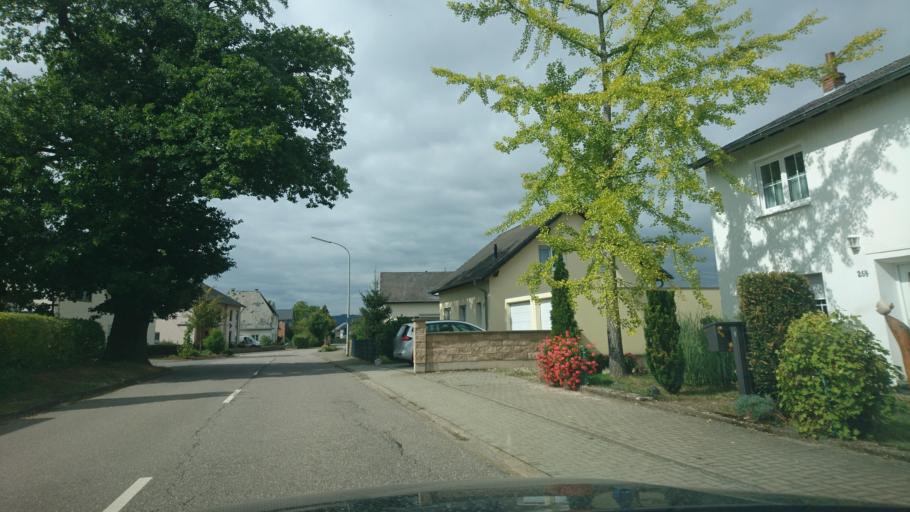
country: DE
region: Rheinland-Pfalz
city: Wiltingen
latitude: 49.6533
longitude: 6.5983
